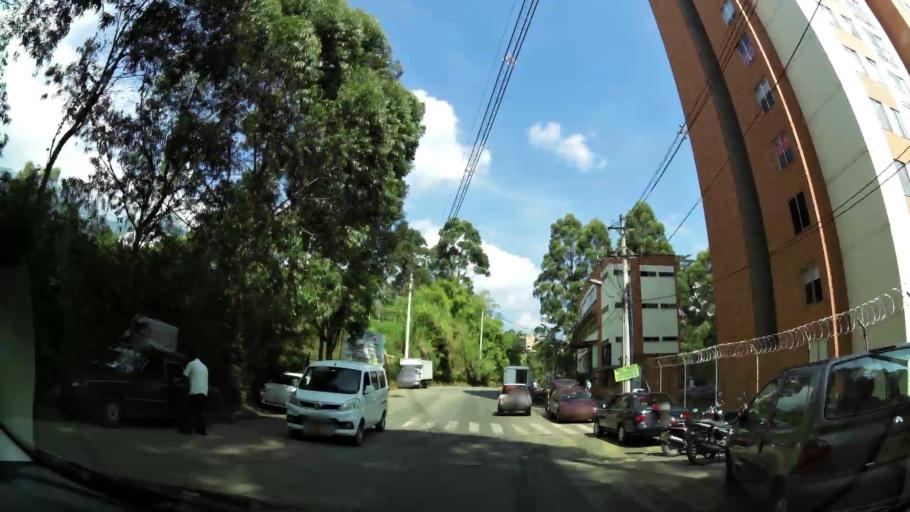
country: CO
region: Antioquia
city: La Estrella
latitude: 6.1677
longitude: -75.6488
